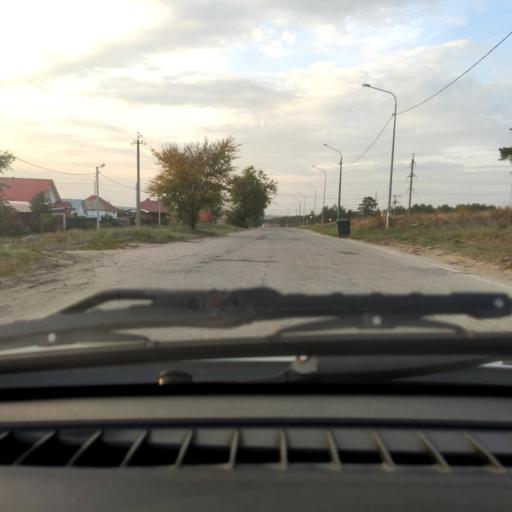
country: RU
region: Samara
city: Zhigulevsk
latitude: 53.4853
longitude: 49.5381
